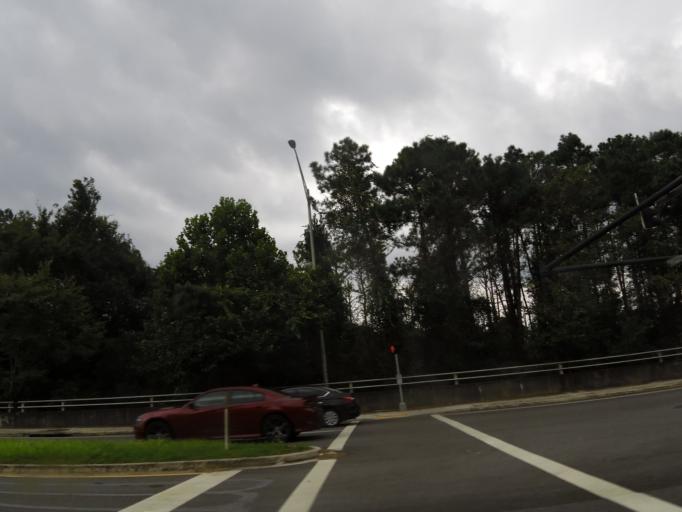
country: US
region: Florida
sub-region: Clay County
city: Bellair-Meadowbrook Terrace
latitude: 30.1952
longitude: -81.7795
